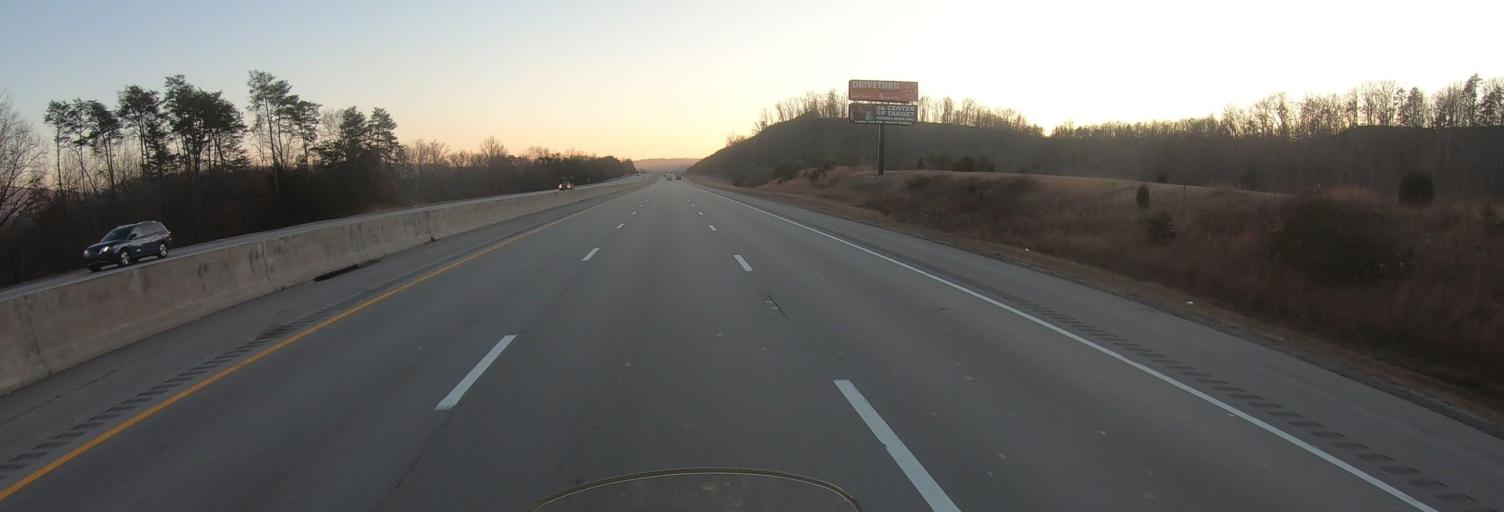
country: US
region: Kentucky
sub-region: Madison County
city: Berea
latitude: 37.4937
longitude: -84.3296
